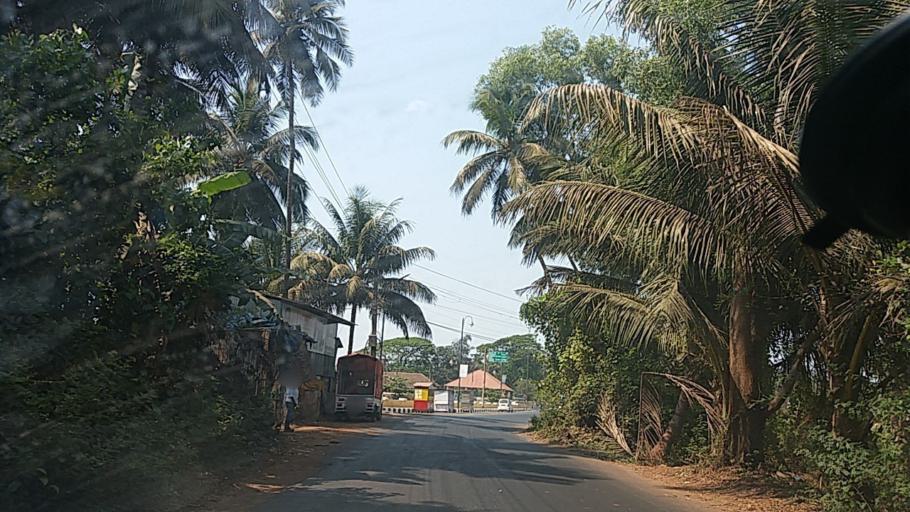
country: IN
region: Goa
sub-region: North Goa
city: Saligao
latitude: 15.5448
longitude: 73.7891
